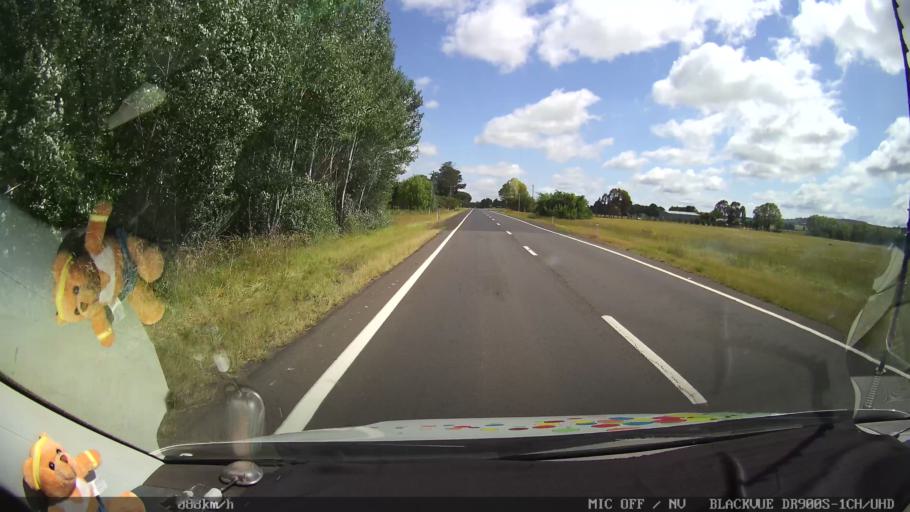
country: AU
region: New South Wales
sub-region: Glen Innes Severn
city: Glen Innes
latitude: -29.8223
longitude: 151.7397
